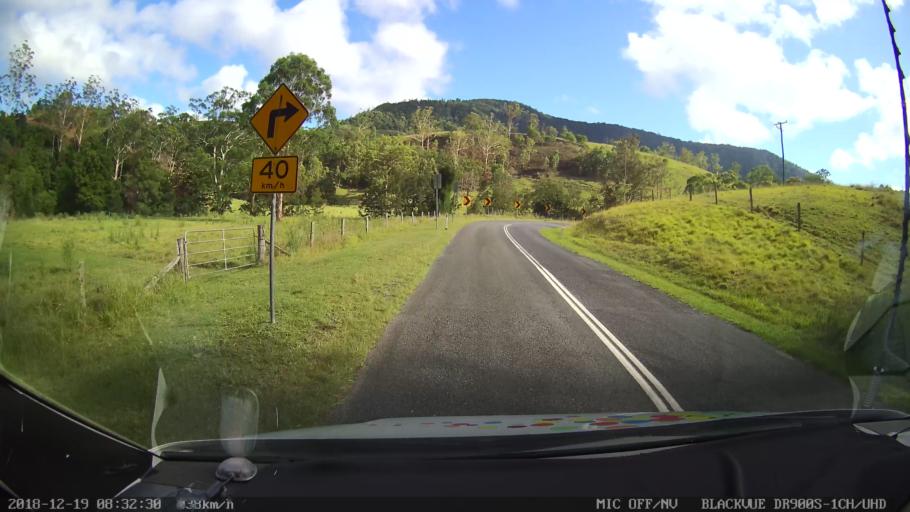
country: AU
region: New South Wales
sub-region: Kyogle
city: Kyogle
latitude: -28.3209
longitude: 152.9422
